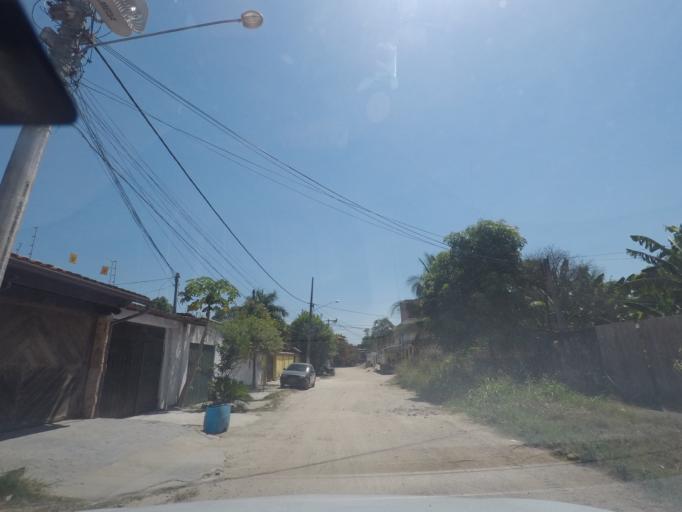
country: BR
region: Rio de Janeiro
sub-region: Niteroi
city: Niteroi
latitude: -22.9373
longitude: -43.0191
